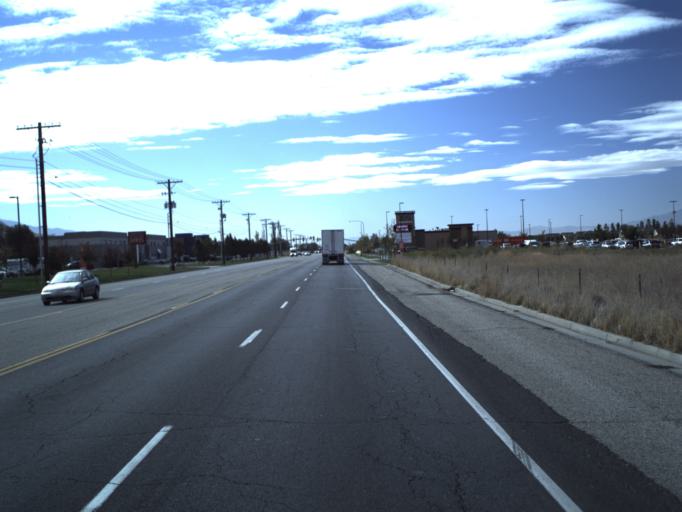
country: US
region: Utah
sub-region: Davis County
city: North Salt Lake
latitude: 40.8561
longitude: -111.9299
